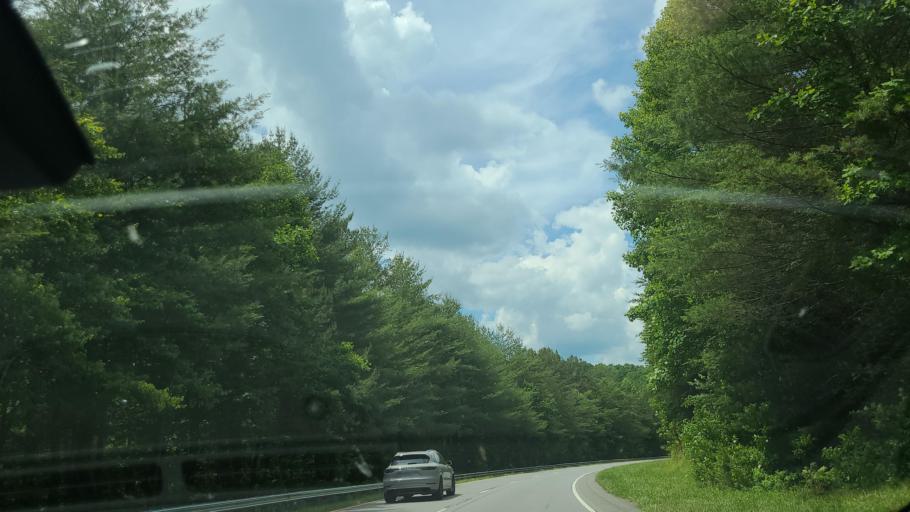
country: US
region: Georgia
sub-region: Fannin County
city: McCaysville
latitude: 35.0118
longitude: -84.2666
